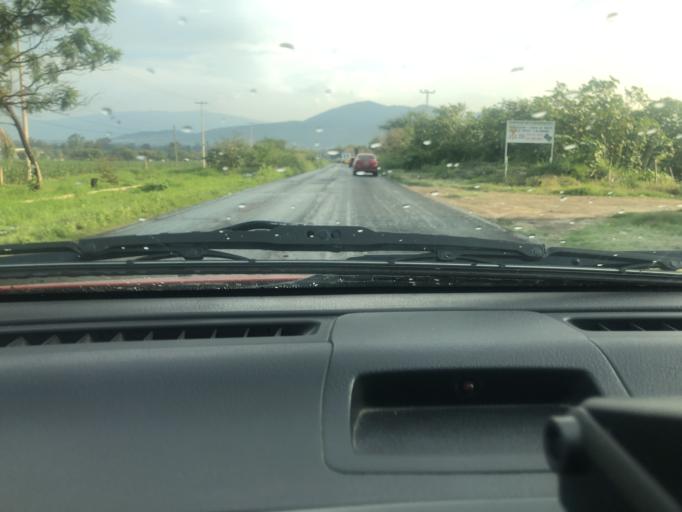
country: MX
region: Jalisco
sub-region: San Pedro Tlaquepaque
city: Santa Anita
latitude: 20.5507
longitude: -103.4199
